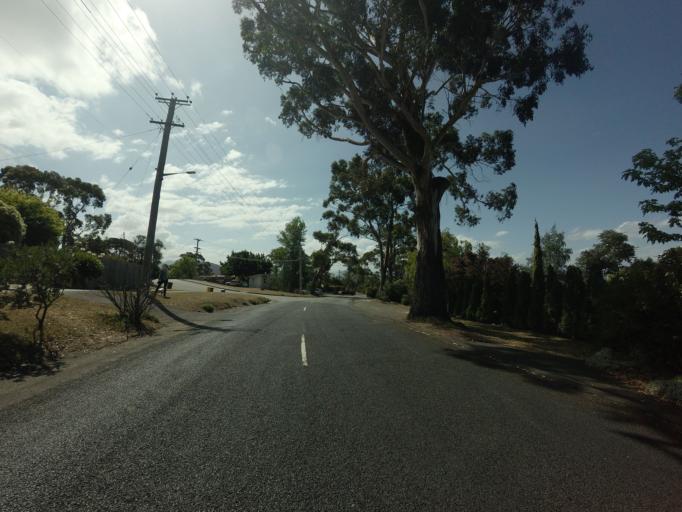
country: AU
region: Tasmania
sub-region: Hobart
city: Dynnyrne
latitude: -42.9146
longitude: 147.3237
